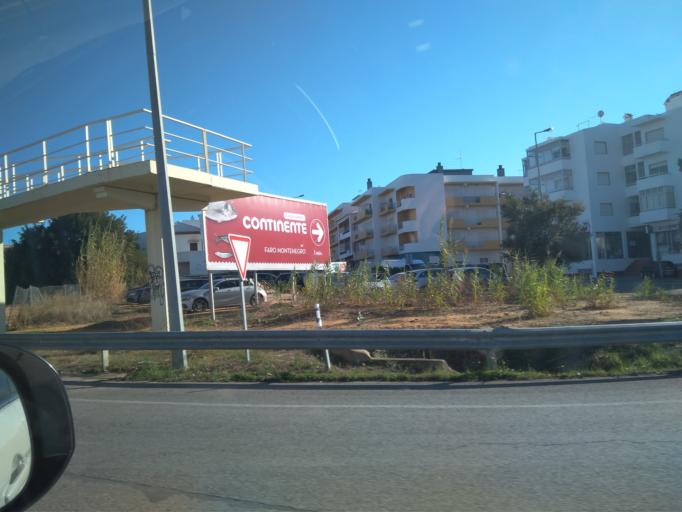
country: PT
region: Faro
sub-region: Faro
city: Faro
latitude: 37.0302
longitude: -7.9683
